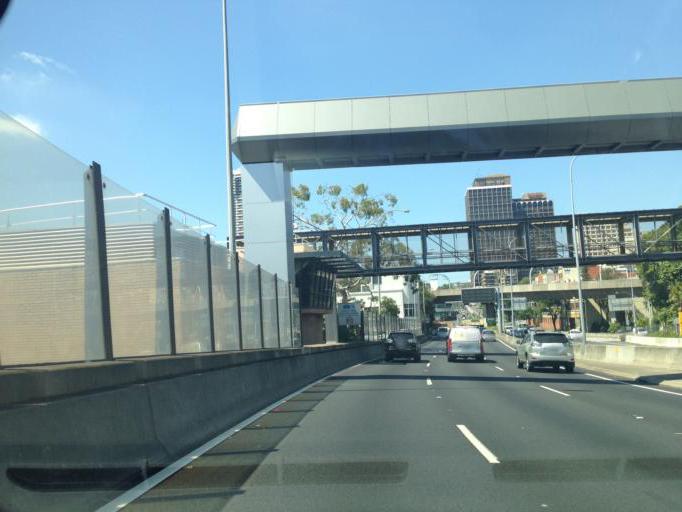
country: AU
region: New South Wales
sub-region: City of Sydney
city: Darlinghurst
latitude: -33.8695
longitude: 151.2186
